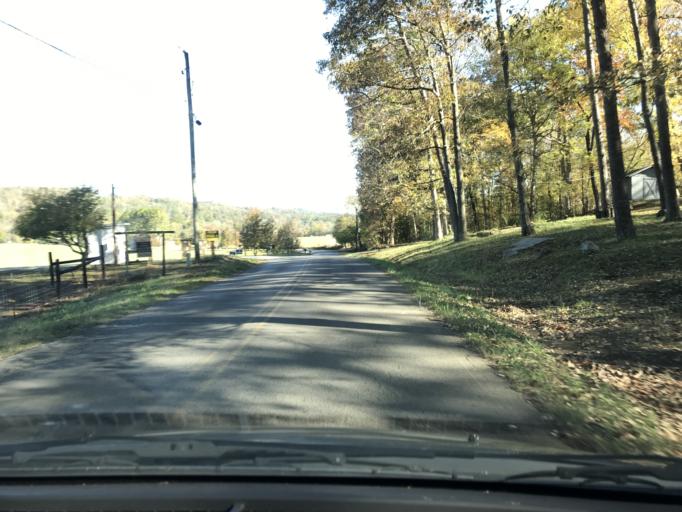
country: US
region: Georgia
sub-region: Dade County
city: Trenton
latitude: 34.8917
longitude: -85.4682
